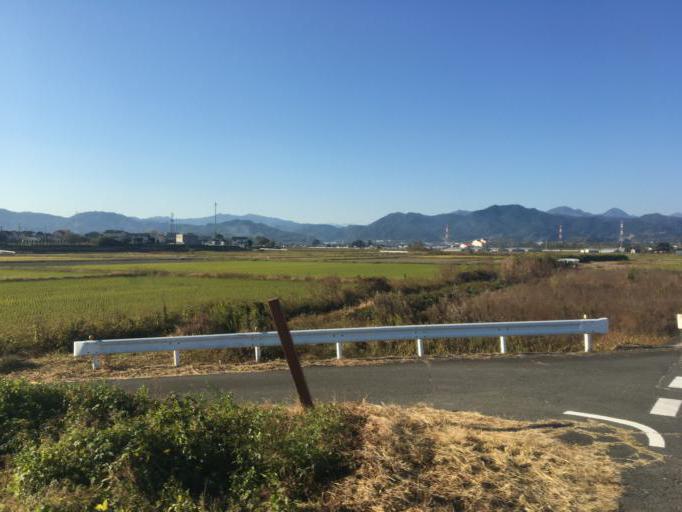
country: JP
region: Gunma
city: Fujioka
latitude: 36.2198
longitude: 139.0977
